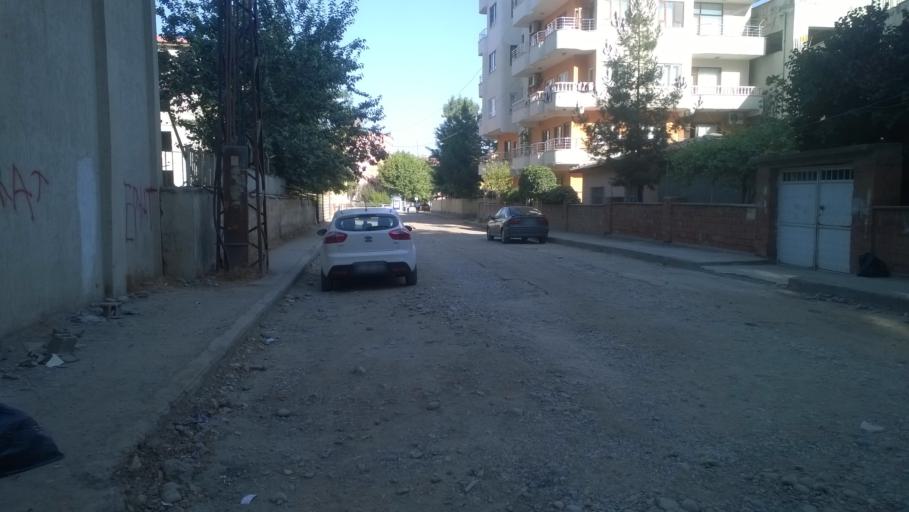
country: TR
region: Batman
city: Batman
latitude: 37.8886
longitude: 41.1278
